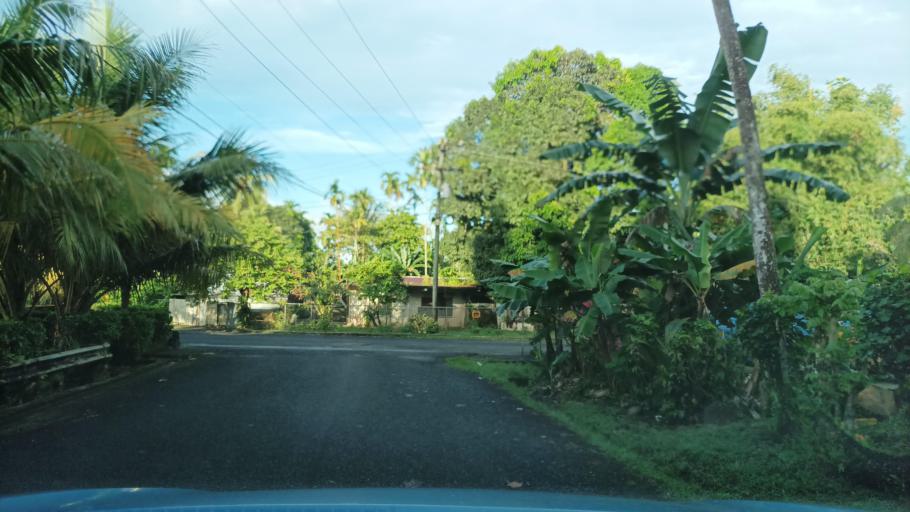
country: FM
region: Pohnpei
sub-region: Kolonia Municipality
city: Kolonia Town
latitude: 6.9668
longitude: 158.2055
